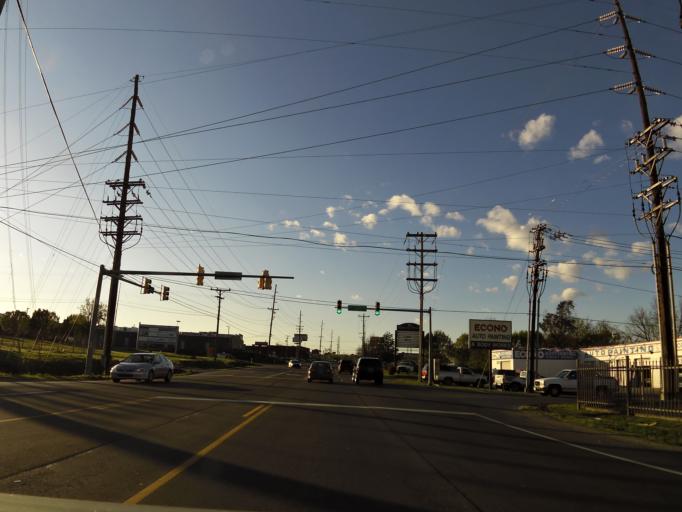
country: US
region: Tennessee
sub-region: Davidson County
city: Goodlettsville
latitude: 36.2936
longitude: -86.6962
